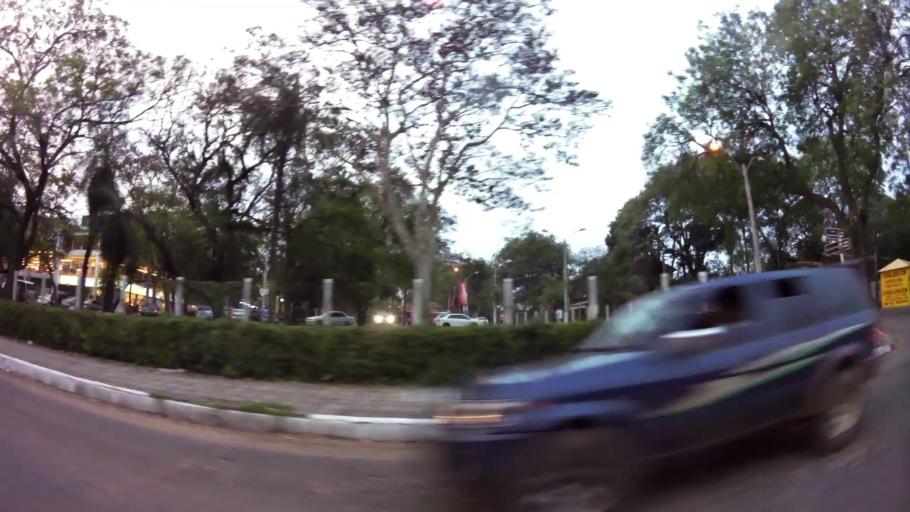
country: PY
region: Central
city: Lambare
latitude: -25.3351
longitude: -57.6123
